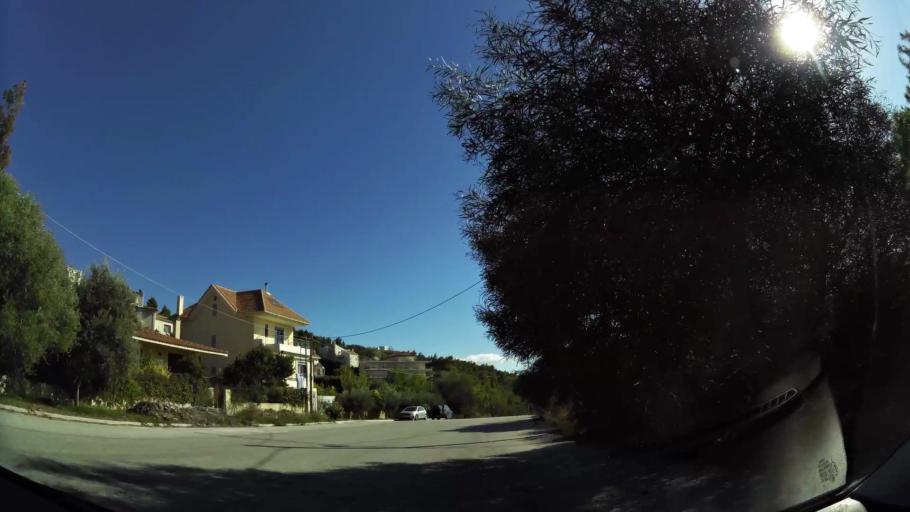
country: GR
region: Attica
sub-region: Nomarchia Anatolikis Attikis
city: Dhrafi
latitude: 38.0170
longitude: 23.9106
